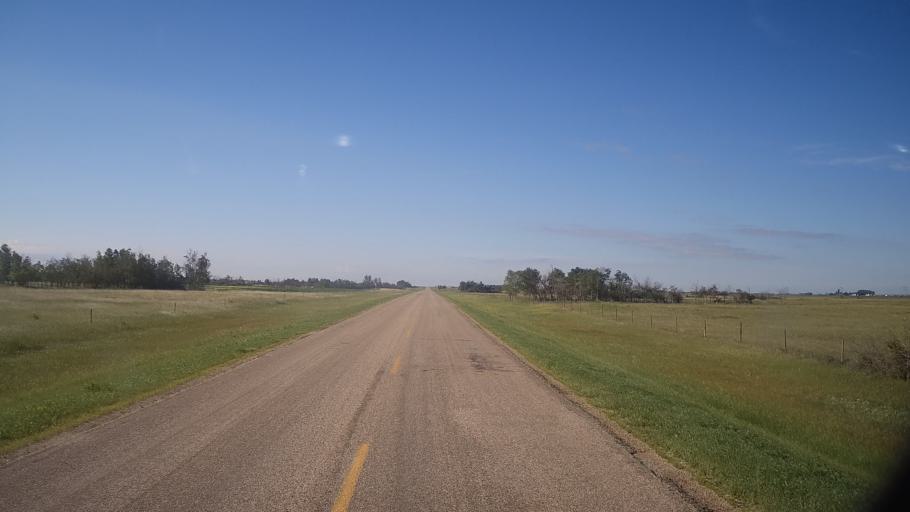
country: CA
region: Saskatchewan
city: Watrous
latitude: 51.7620
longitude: -105.2867
